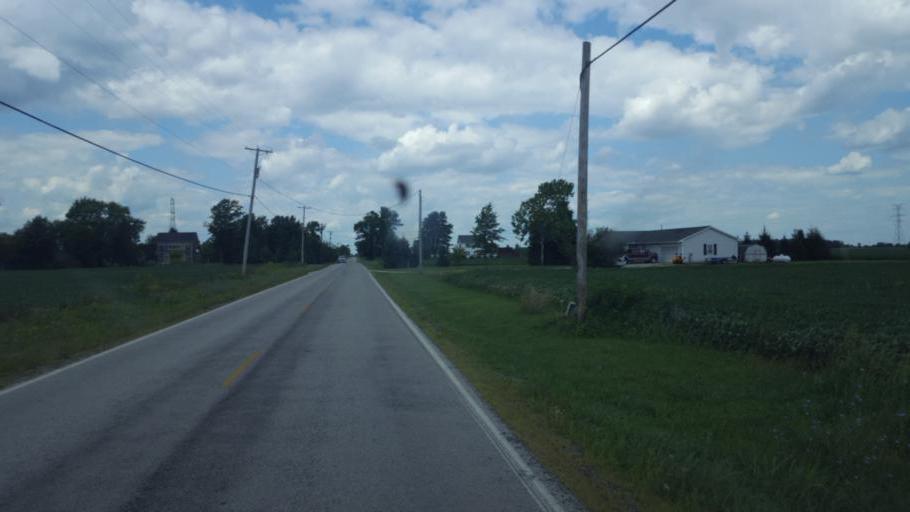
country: US
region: Ohio
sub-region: Ottawa County
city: Elmore
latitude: 41.5499
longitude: -83.2802
